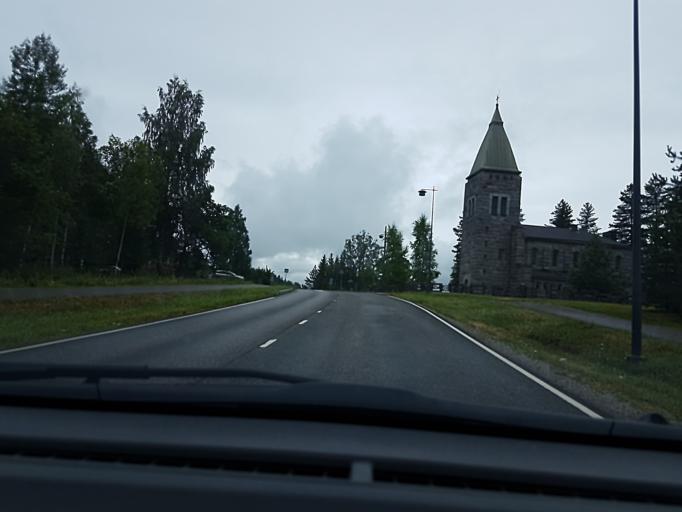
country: FI
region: Uusimaa
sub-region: Helsinki
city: Pornainen
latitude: 60.4749
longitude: 25.3758
